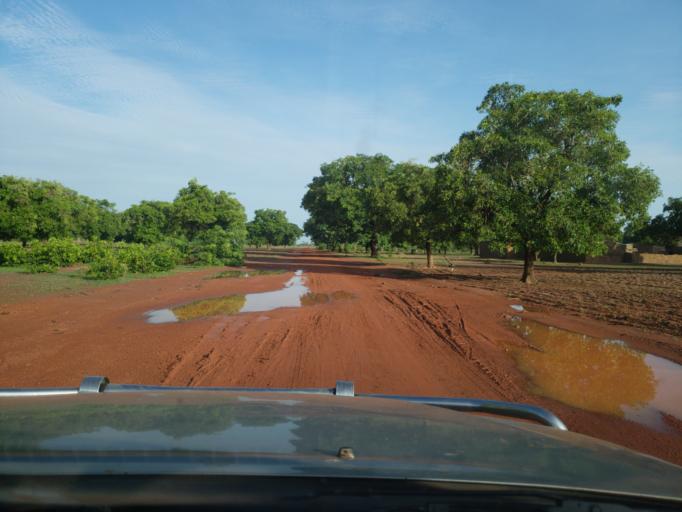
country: ML
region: Sikasso
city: Koutiala
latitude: 12.4277
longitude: -5.6012
